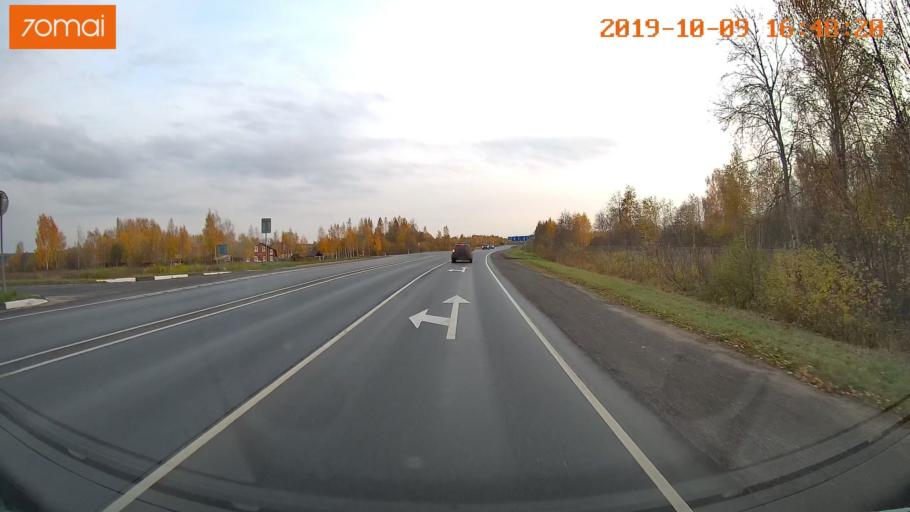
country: RU
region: Kostroma
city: Volgorechensk
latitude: 57.4285
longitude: 41.1901
